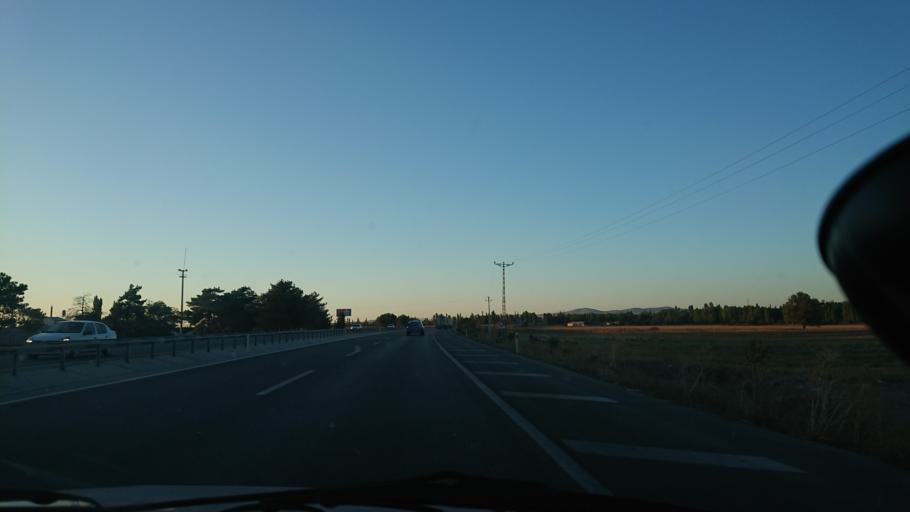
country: TR
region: Eskisehir
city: Mahmudiye
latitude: 39.5608
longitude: 30.9167
